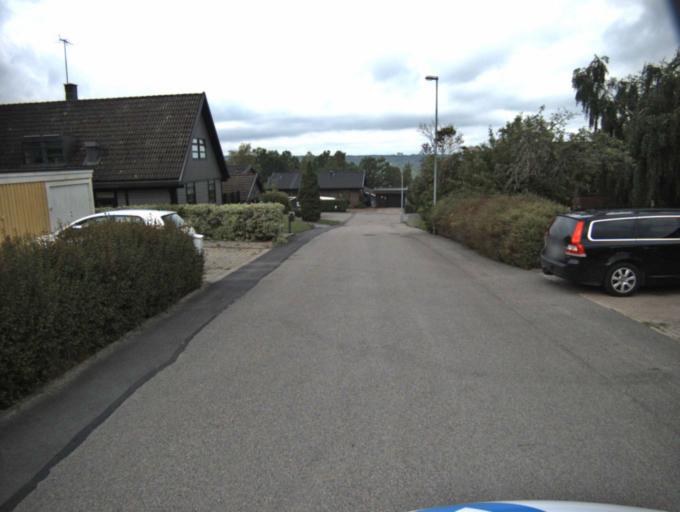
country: SE
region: Vaestra Goetaland
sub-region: Ulricehamns Kommun
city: Ulricehamn
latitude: 57.7772
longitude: 13.4147
